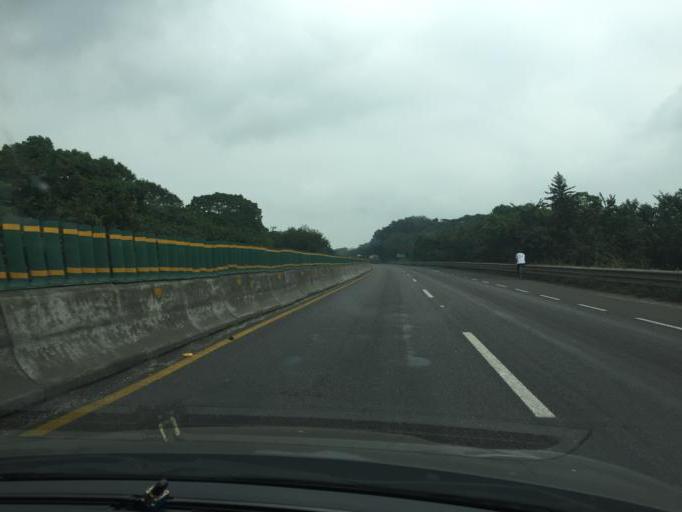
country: MX
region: Veracruz
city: Villa Nanchital
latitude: 18.0469
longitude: -94.3335
